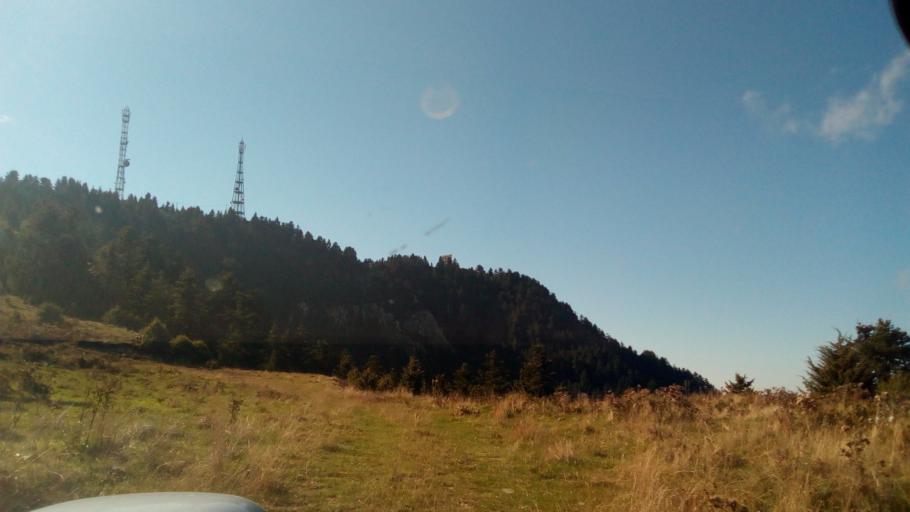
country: GR
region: Central Greece
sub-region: Nomos Fokidos
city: Lidoriki
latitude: 38.6056
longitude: 21.9656
